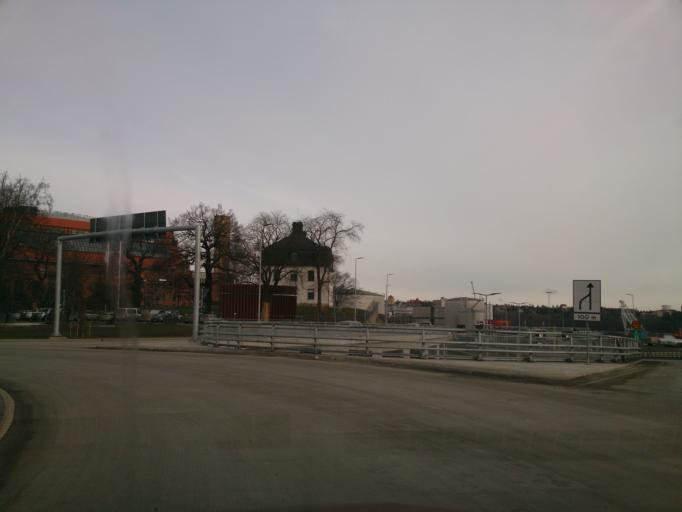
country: SE
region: Stockholm
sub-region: Stockholms Kommun
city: OEstermalm
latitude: 59.3508
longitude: 18.1042
